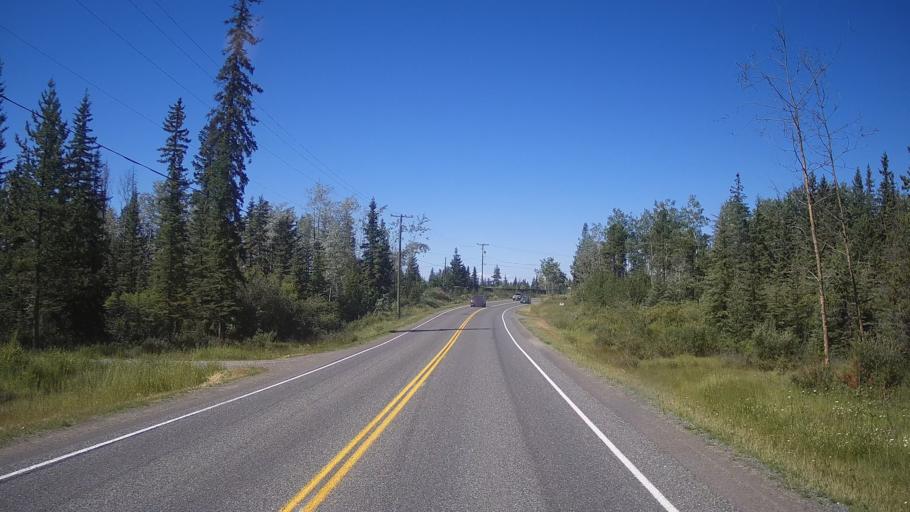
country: CA
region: British Columbia
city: Cache Creek
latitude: 51.5518
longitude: -121.2284
